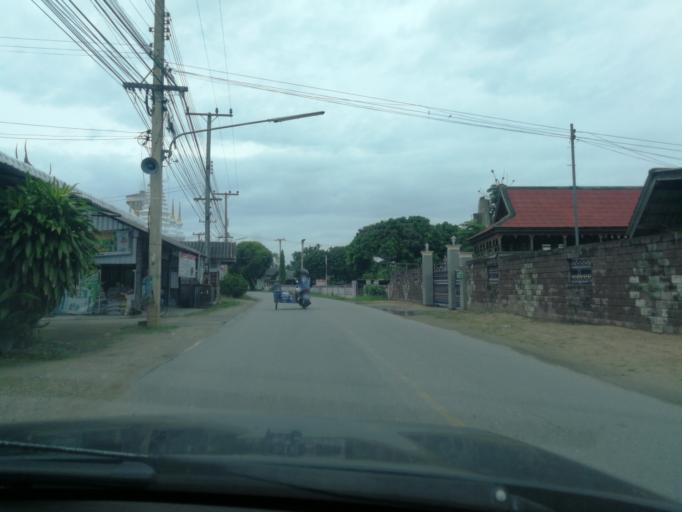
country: TH
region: Chiang Mai
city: San Pa Tong
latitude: 18.5992
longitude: 98.9104
